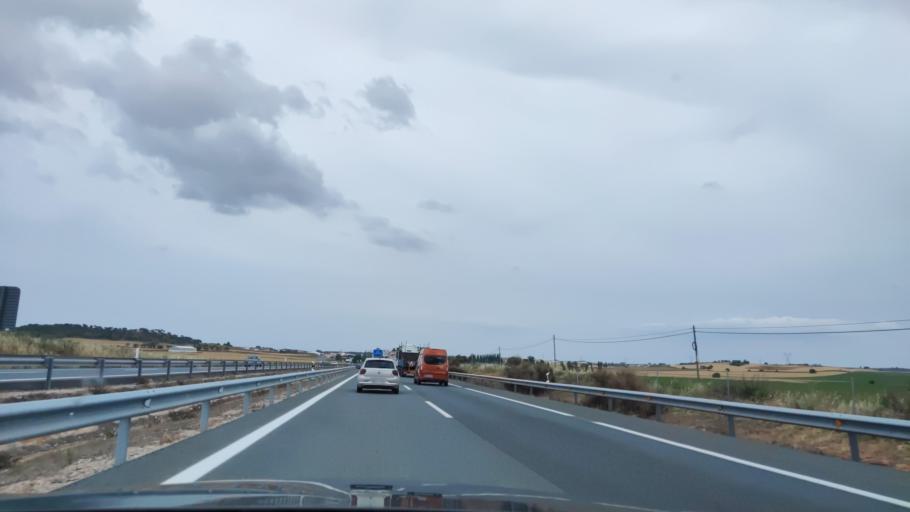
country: ES
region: Castille-La Mancha
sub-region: Provincia de Cuenca
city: Honrubia
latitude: 39.6223
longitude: -2.3008
